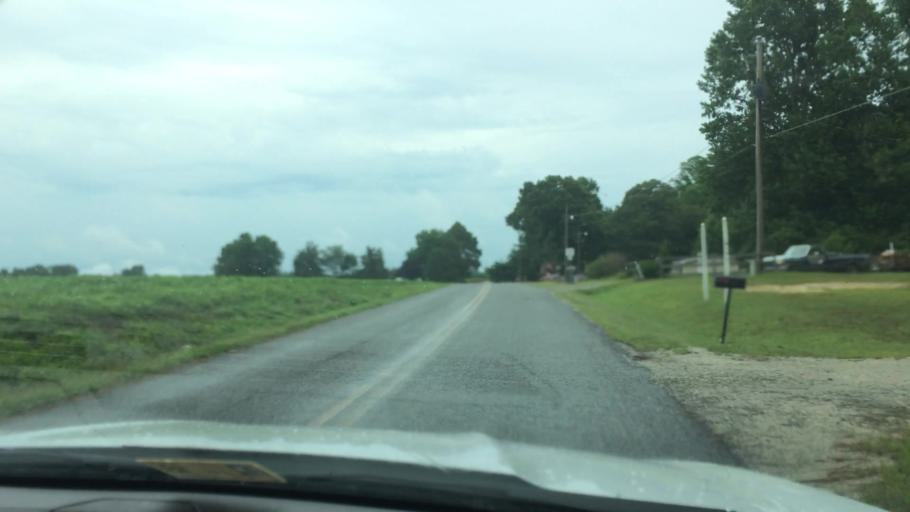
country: US
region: Virginia
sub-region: King William County
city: West Point
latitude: 37.5286
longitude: -76.7446
